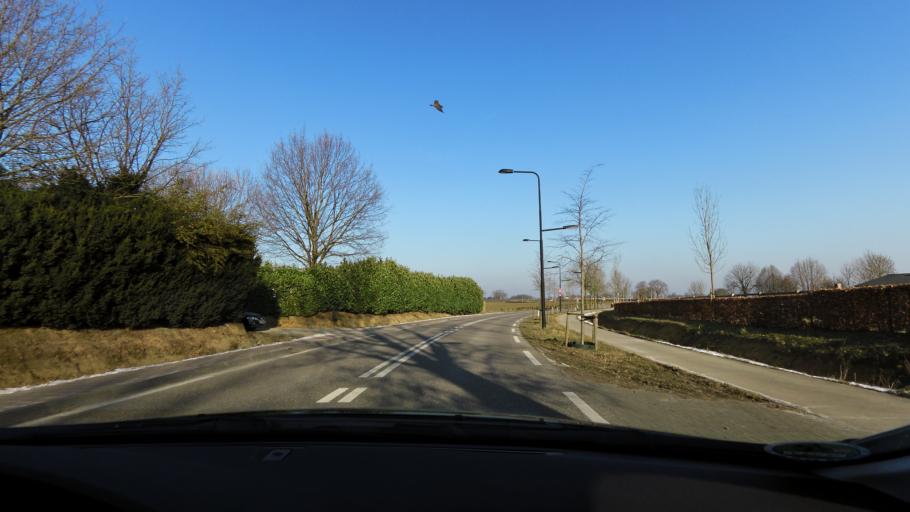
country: NL
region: Limburg
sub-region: Valkenburg aan de Geul
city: Broekhem
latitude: 50.8920
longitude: 5.8366
